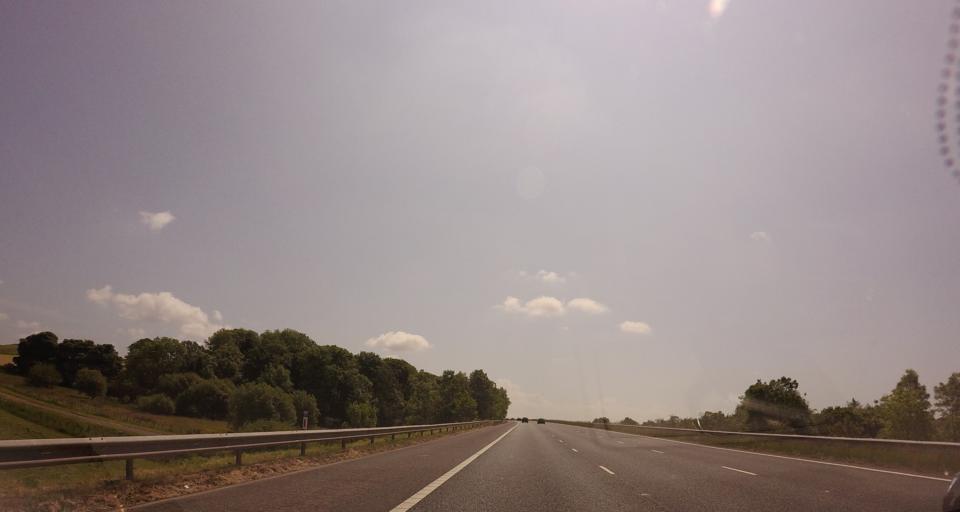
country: GB
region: Scotland
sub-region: Dumfries and Galloway
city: Lockerbie
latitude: 55.0844
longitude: -3.3170
